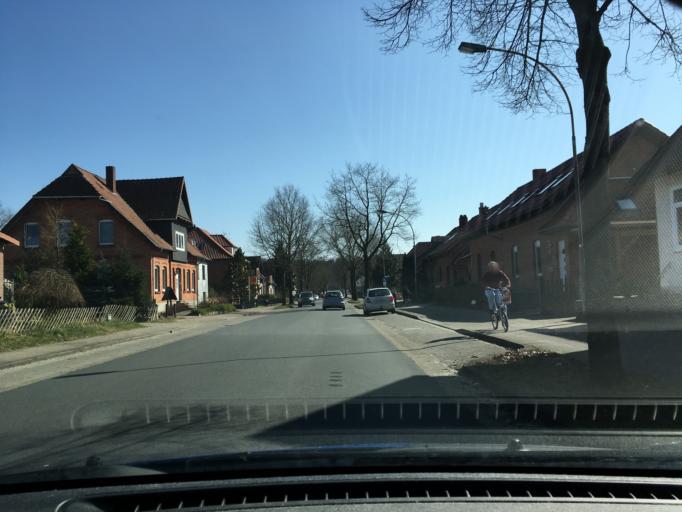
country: DE
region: Lower Saxony
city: Unterluss
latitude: 52.8377
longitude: 10.2972
